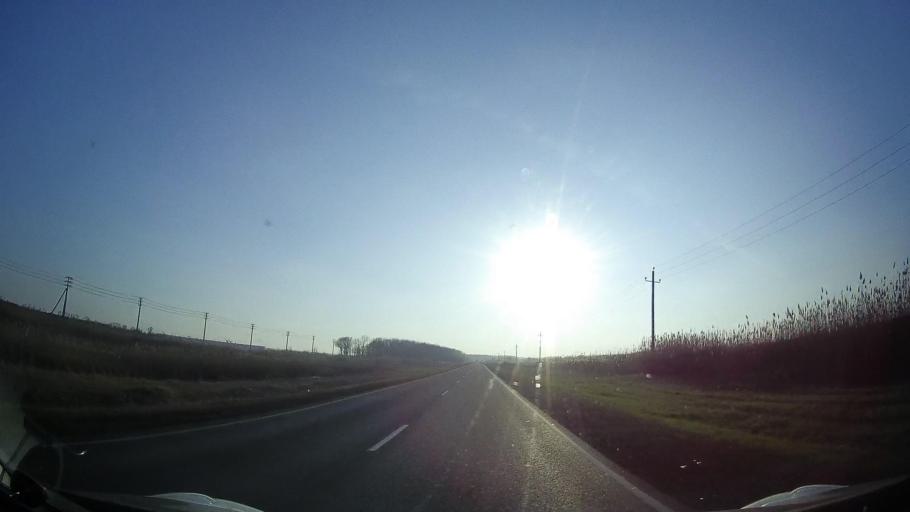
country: RU
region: Rostov
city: Ol'ginskaya
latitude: 47.1451
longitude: 39.9053
